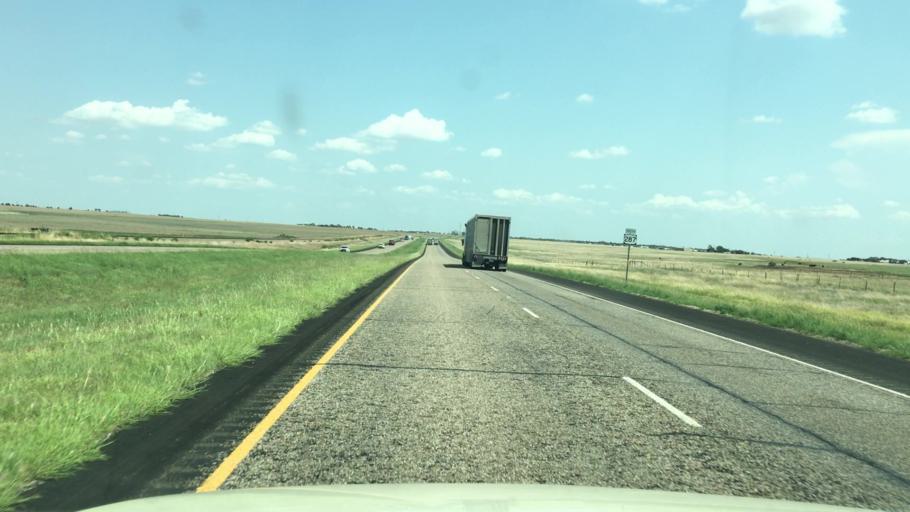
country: US
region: Texas
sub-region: Armstrong County
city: Claude
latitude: 35.1299
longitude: -101.4118
